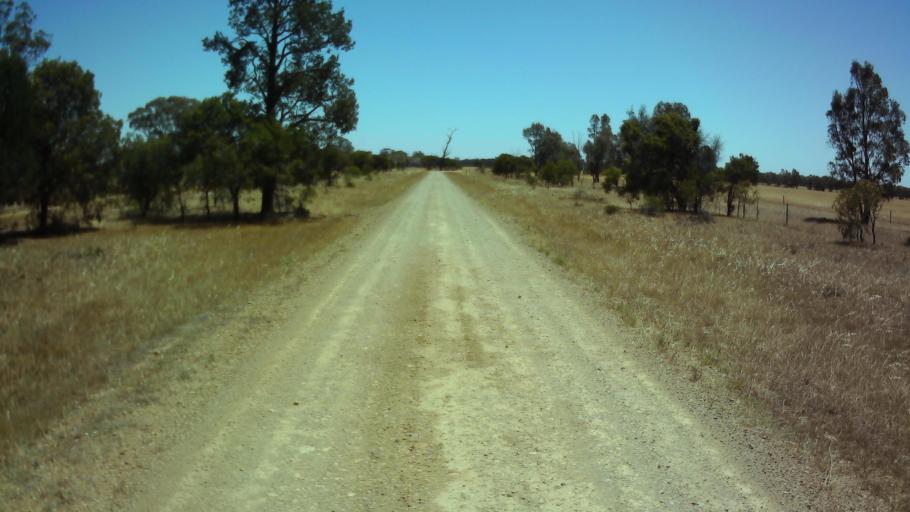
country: AU
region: New South Wales
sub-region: Weddin
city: Grenfell
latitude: -33.9872
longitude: 147.9298
